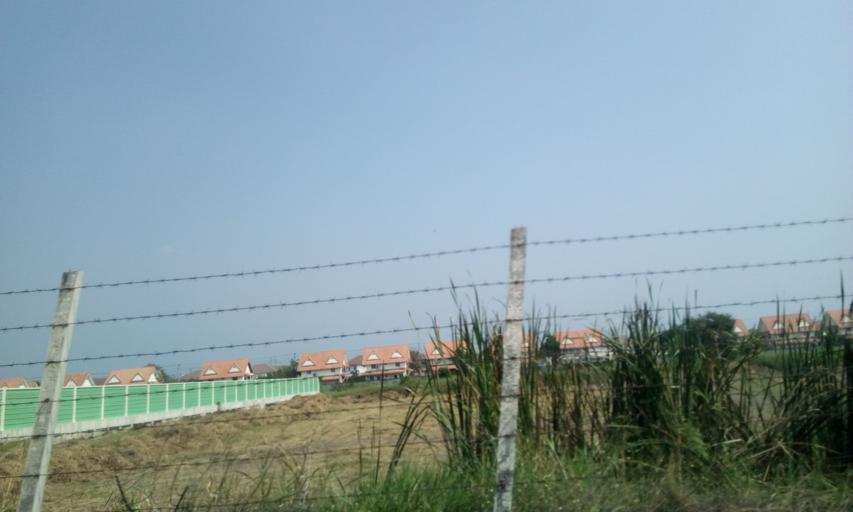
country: TH
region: Pathum Thani
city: Ban Rangsit
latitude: 14.0232
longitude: 100.7592
